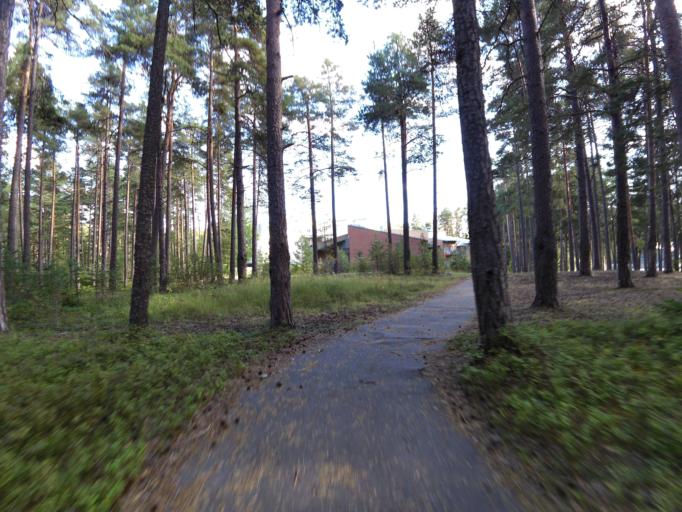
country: SE
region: Gaevleborg
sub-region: Gavle Kommun
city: Gavle
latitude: 60.7108
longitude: 17.1656
